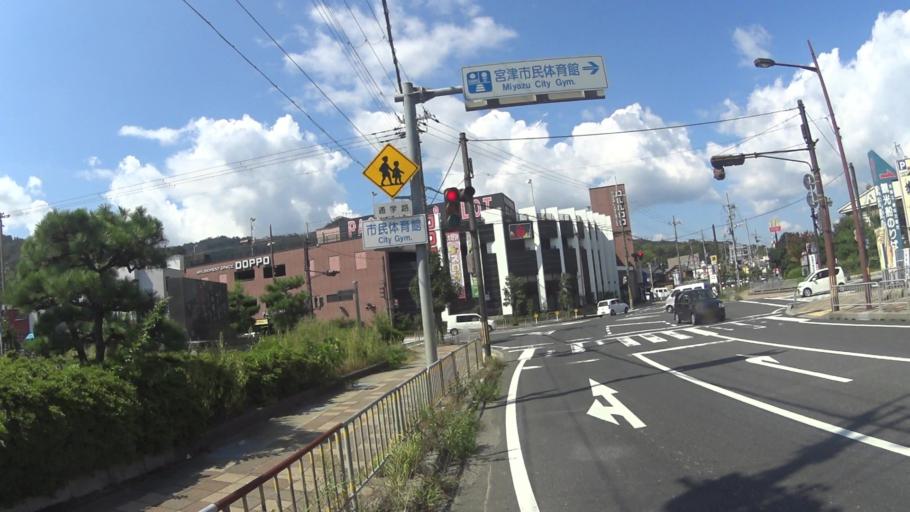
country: JP
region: Kyoto
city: Miyazu
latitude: 35.5384
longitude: 135.1926
